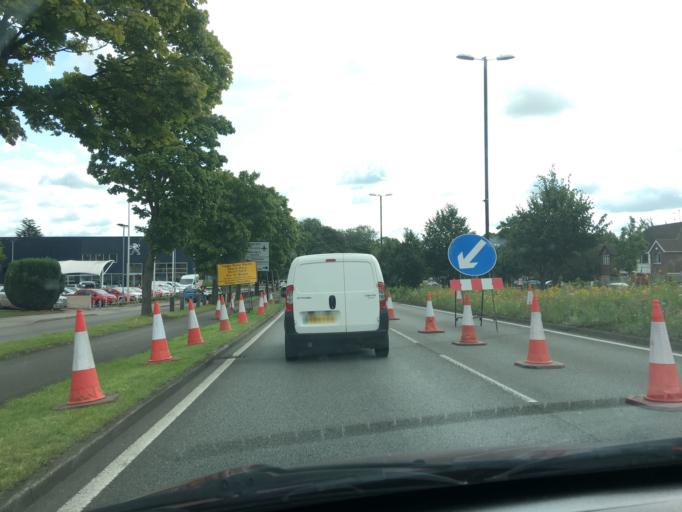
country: GB
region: England
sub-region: Coventry
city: Coventry
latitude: 52.3803
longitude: -1.5188
